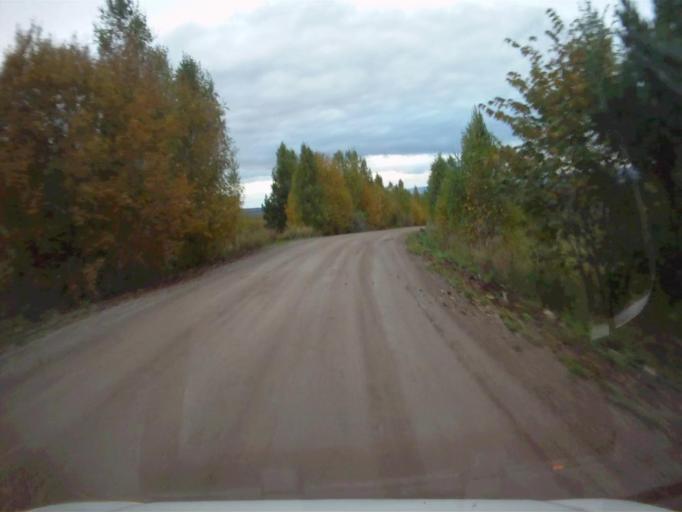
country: RU
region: Sverdlovsk
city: Mikhaylovsk
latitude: 56.2019
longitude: 59.2007
